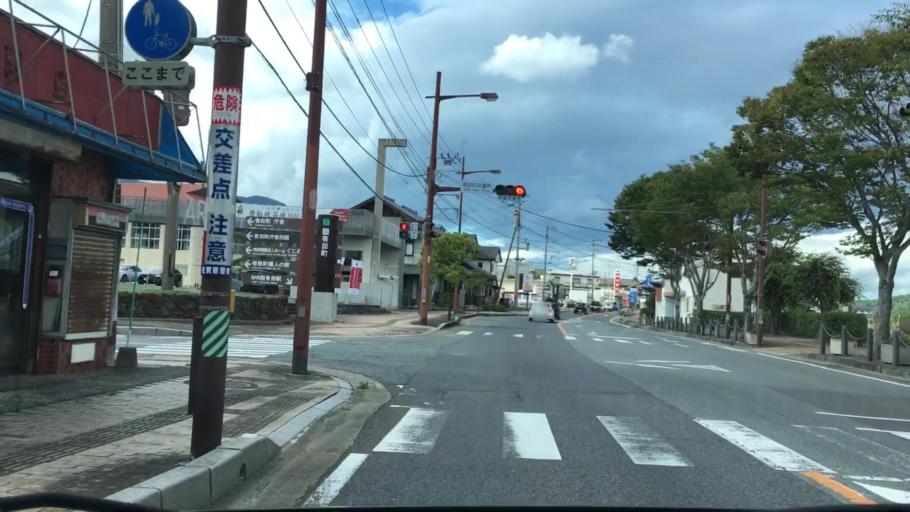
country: JP
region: Saga Prefecture
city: Imaricho-ko
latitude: 33.2103
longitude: 129.8498
